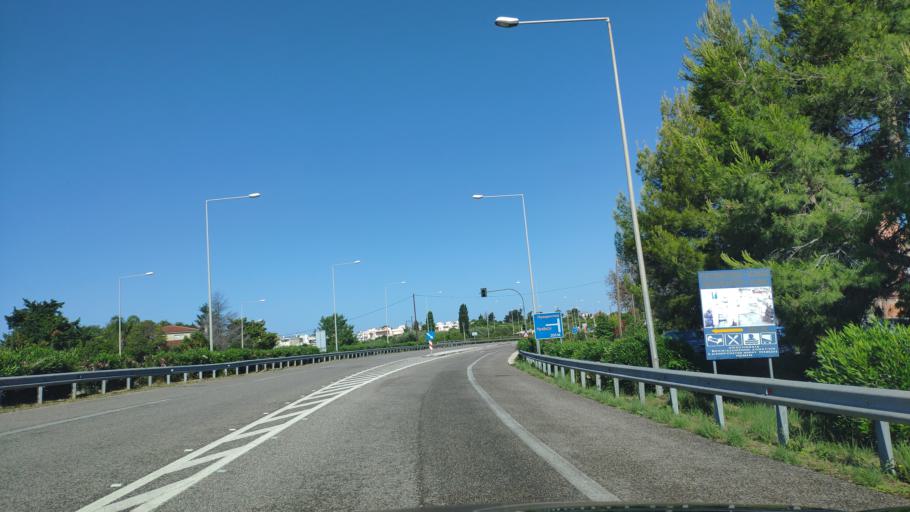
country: GR
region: Epirus
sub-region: Nomos Prevezis
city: Preveza
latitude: 38.9485
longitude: 20.7408
